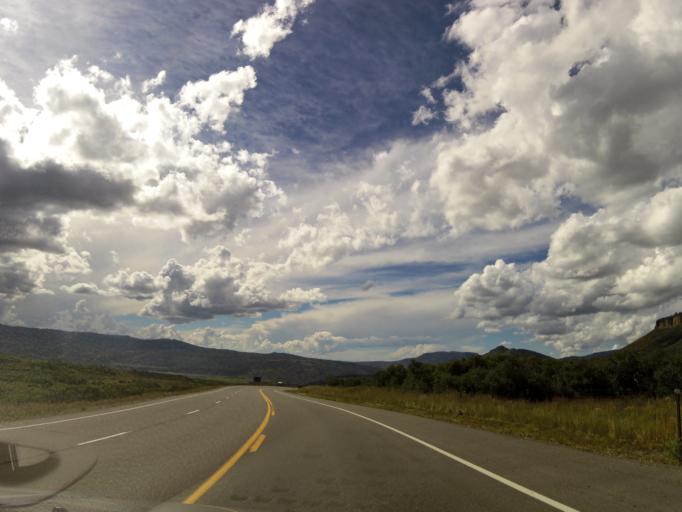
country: US
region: Colorado
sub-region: Hinsdale County
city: Lake City
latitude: 38.3903
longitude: -107.4396
